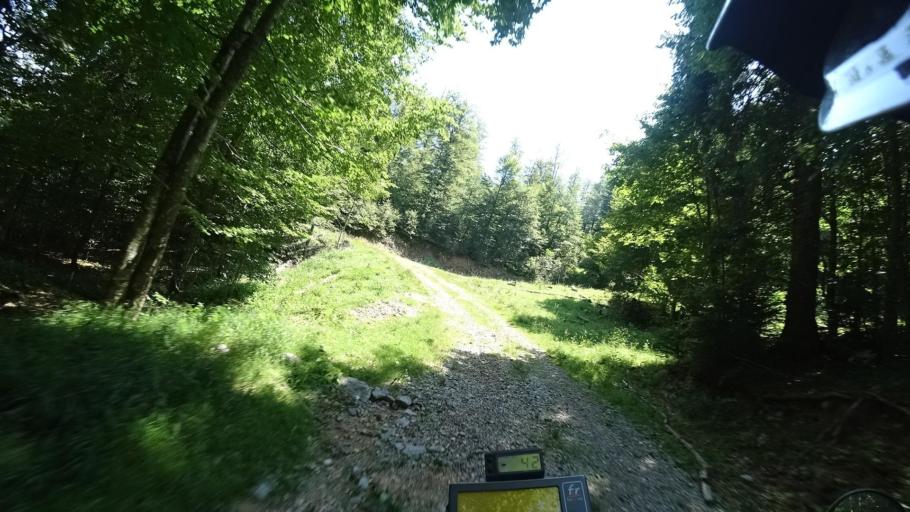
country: HR
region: Primorsko-Goranska
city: Bribir
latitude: 45.2580
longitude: 14.8638
